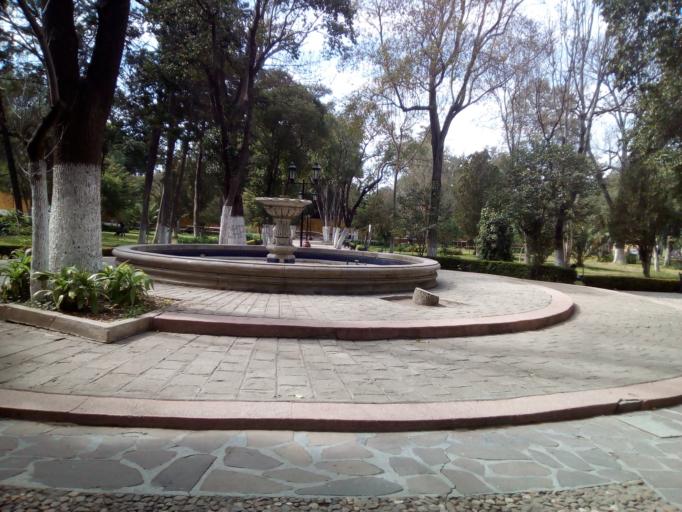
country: MX
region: Guanajuato
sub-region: San Luis de la Paz
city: San Luis de la Paz
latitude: 21.2989
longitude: -100.5103
